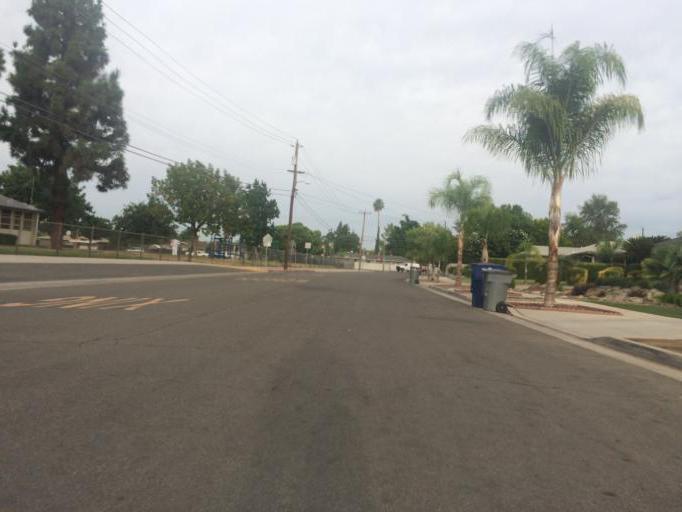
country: US
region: California
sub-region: Fresno County
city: Fresno
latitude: 36.7686
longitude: -119.7438
